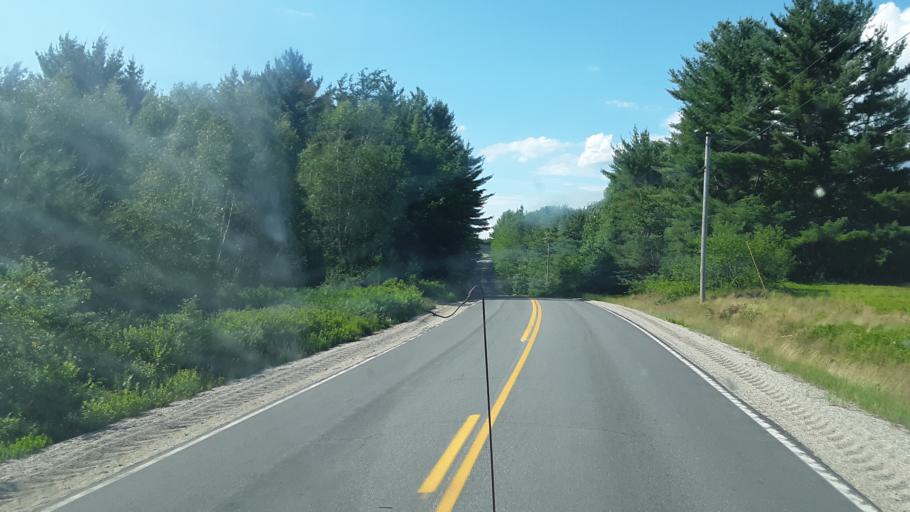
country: US
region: Maine
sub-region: Washington County
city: Cherryfield
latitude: 44.7574
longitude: -68.0247
